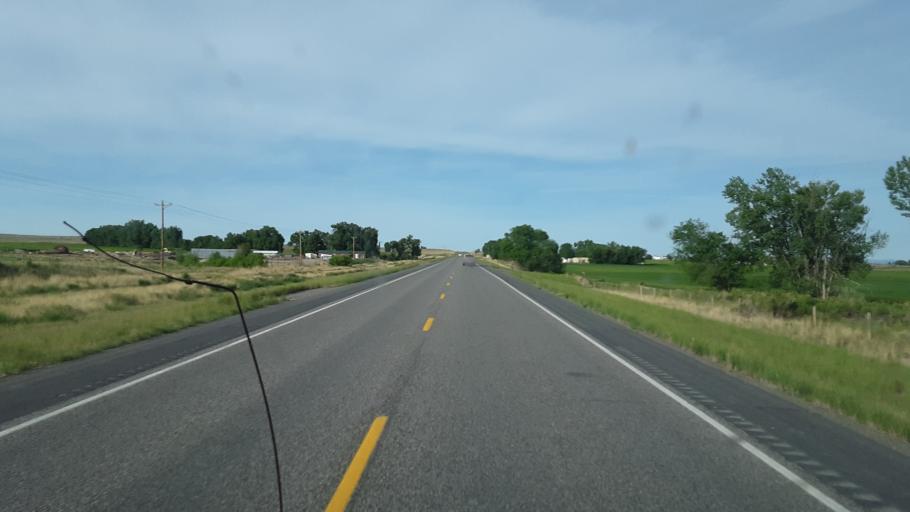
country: US
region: Wyoming
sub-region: Fremont County
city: Riverton
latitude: 43.1746
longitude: -108.2561
